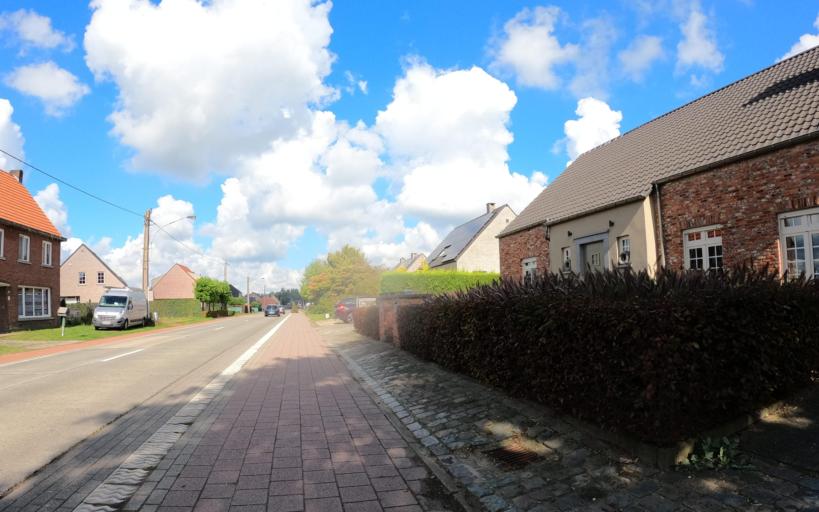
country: BE
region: Flanders
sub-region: Provincie Antwerpen
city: Rijkevorsel
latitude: 51.3229
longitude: 4.7729
